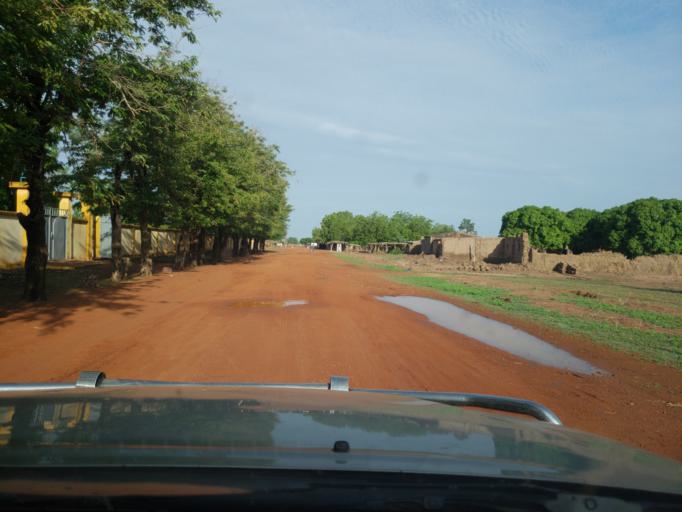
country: ML
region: Sikasso
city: Koutiala
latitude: 12.4225
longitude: -5.6842
